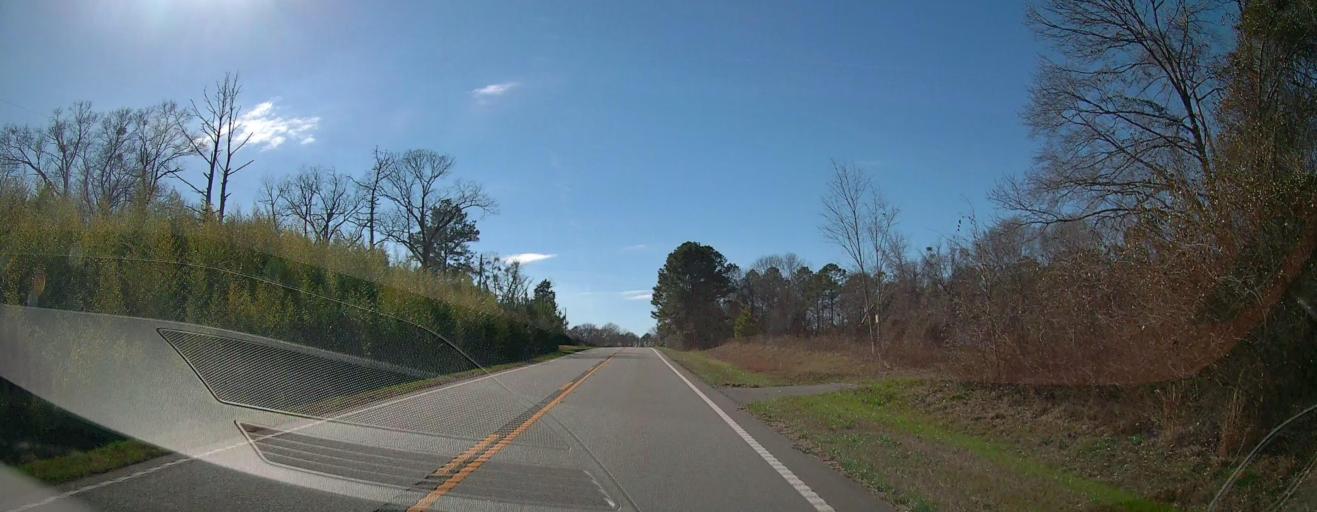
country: US
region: Georgia
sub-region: Macon County
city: Oglethorpe
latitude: 32.3516
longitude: -84.1640
